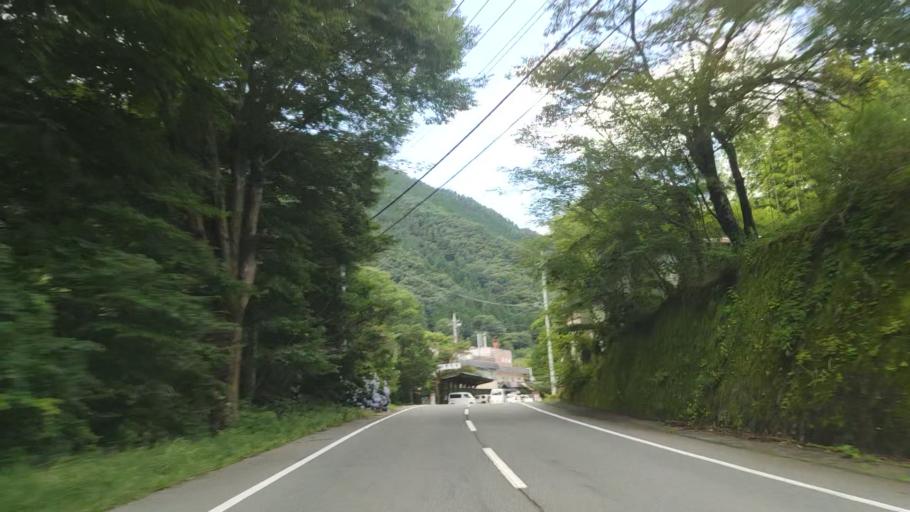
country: JP
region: Yamanashi
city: Enzan
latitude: 35.7944
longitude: 138.7394
